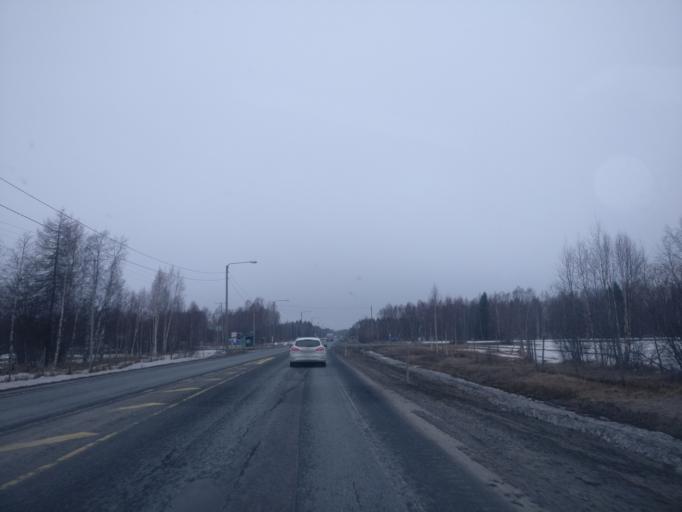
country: FI
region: Lapland
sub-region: Kemi-Tornio
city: Simo
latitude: 65.6693
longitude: 24.9296
